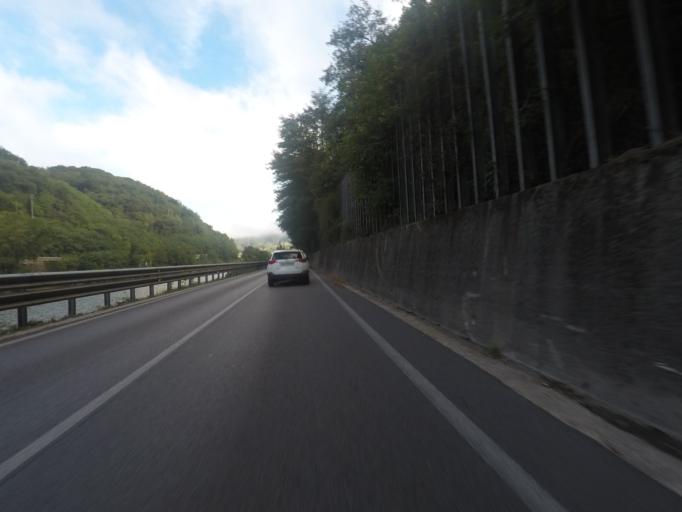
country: IT
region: Tuscany
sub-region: Provincia di Lucca
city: Borgo a Mozzano
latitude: 43.9902
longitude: 10.5531
